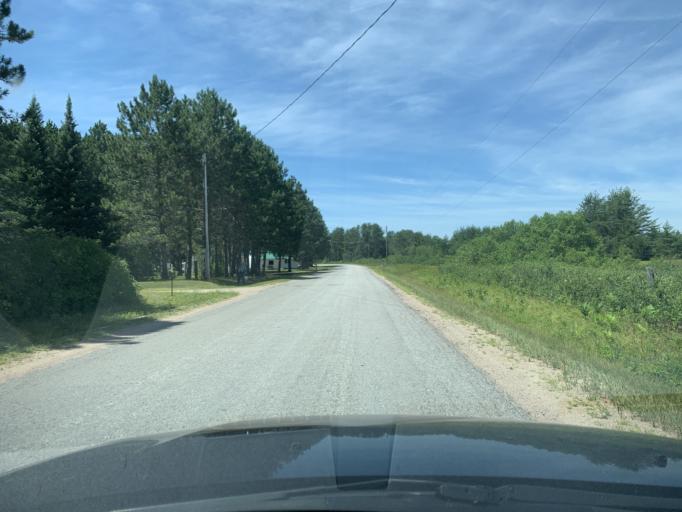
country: CA
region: Ontario
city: Petawawa
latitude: 45.6605
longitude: -77.5889
